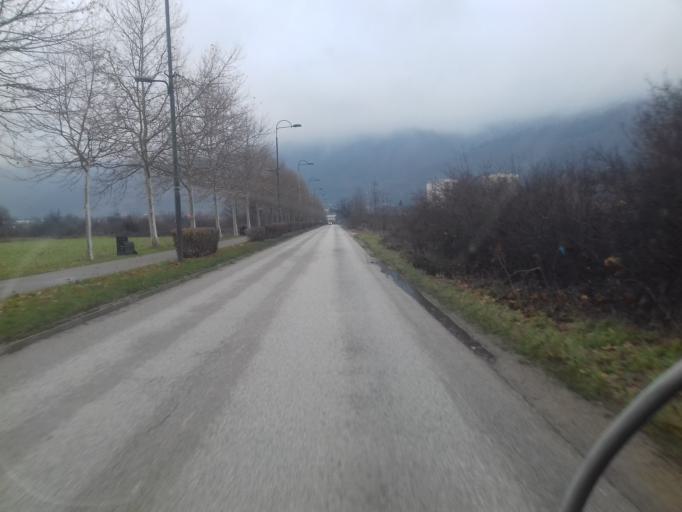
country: BA
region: Federation of Bosnia and Herzegovina
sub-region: Kanton Sarajevo
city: Sarajevo
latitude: 43.8038
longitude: 18.3121
